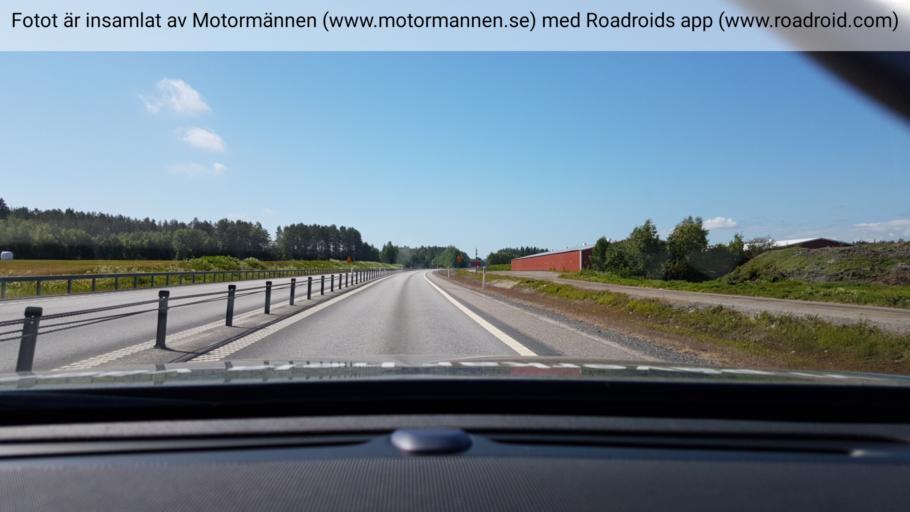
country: SE
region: Vaesterbotten
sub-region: Umea Kommun
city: Roback
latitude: 63.7614
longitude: 20.1676
